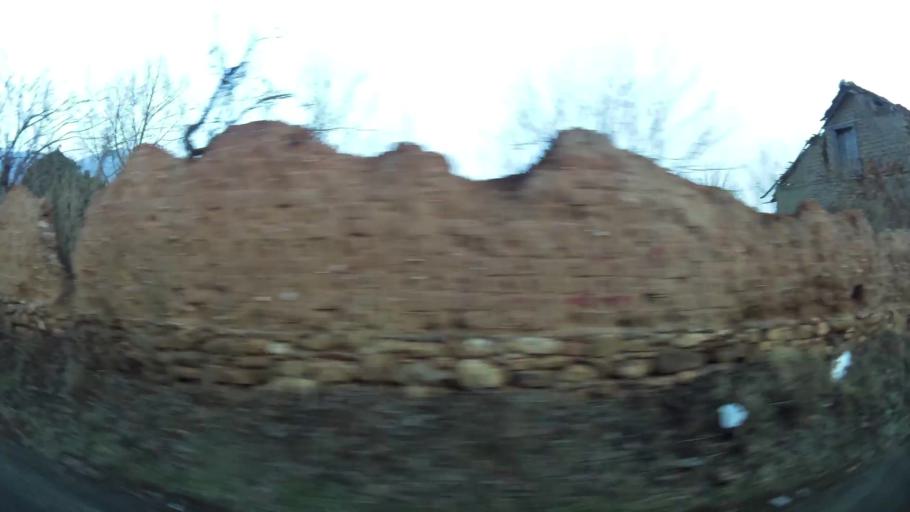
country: MK
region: Aracinovo
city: Arachinovo
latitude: 42.0336
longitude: 21.5466
